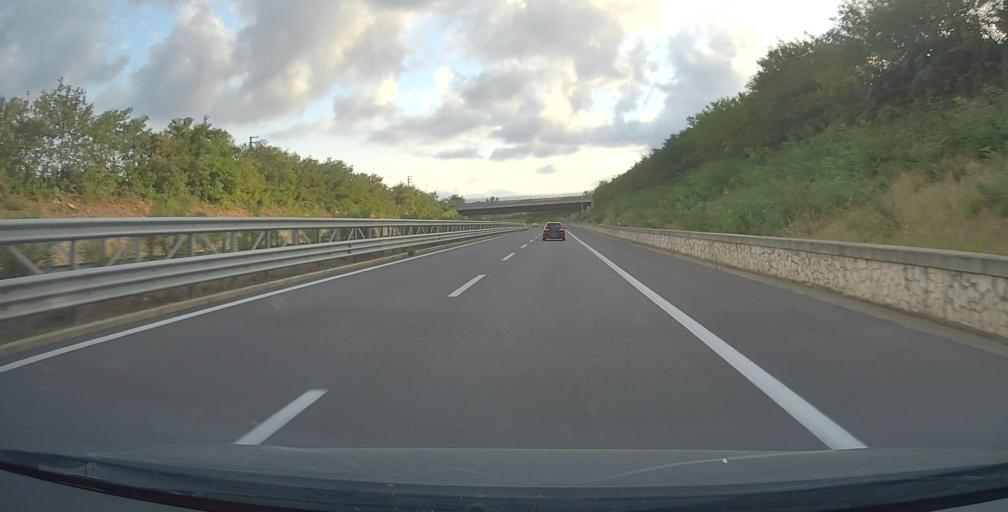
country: IT
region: Calabria
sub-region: Provincia di Catanzaro
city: Acconia
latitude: 38.8657
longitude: 16.2790
